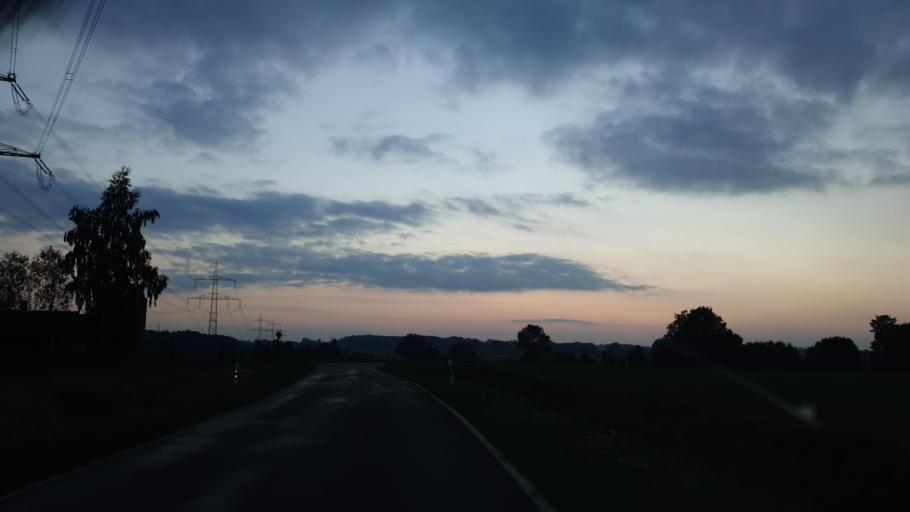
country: DE
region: North Rhine-Westphalia
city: Loehne
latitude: 52.2336
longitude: 8.6898
